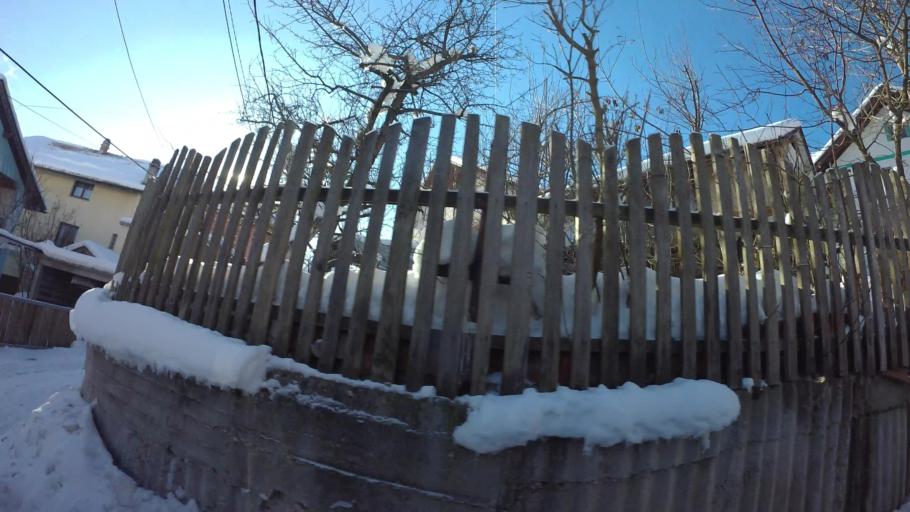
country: BA
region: Federation of Bosnia and Herzegovina
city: Kobilja Glava
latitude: 43.8927
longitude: 18.4090
